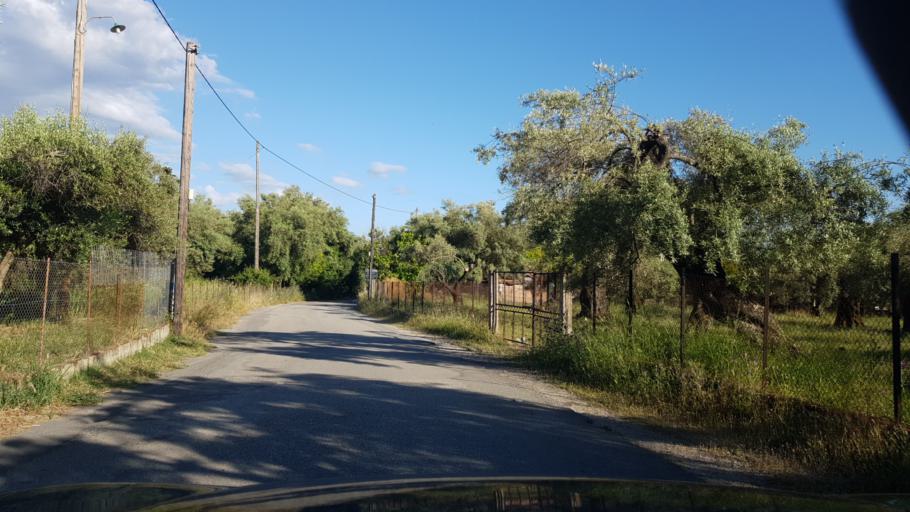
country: GR
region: Ionian Islands
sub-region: Lefkada
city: Nidri
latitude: 38.7137
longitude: 20.7021
